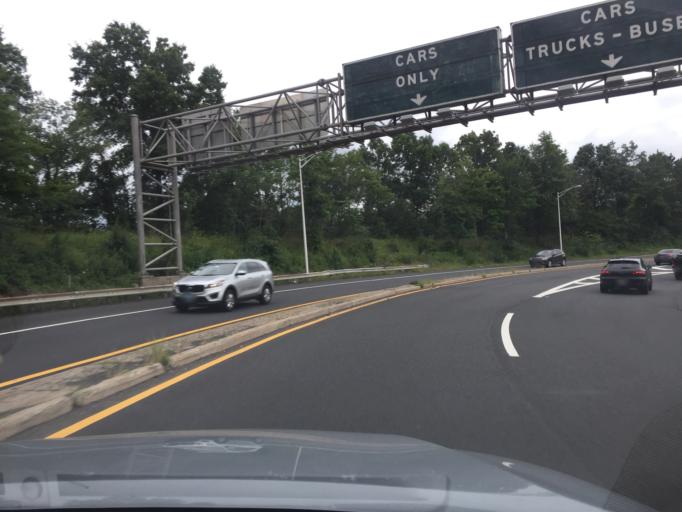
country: US
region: New Jersey
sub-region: Middlesex County
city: Piscataway
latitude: 40.4777
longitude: -74.4029
